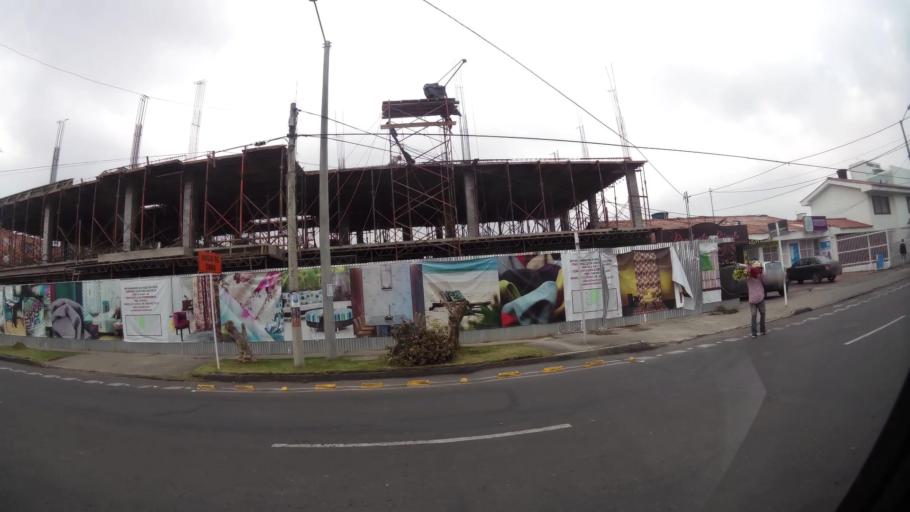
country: CO
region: Bogota D.C.
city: Barrio San Luis
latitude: 4.7242
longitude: -74.0468
